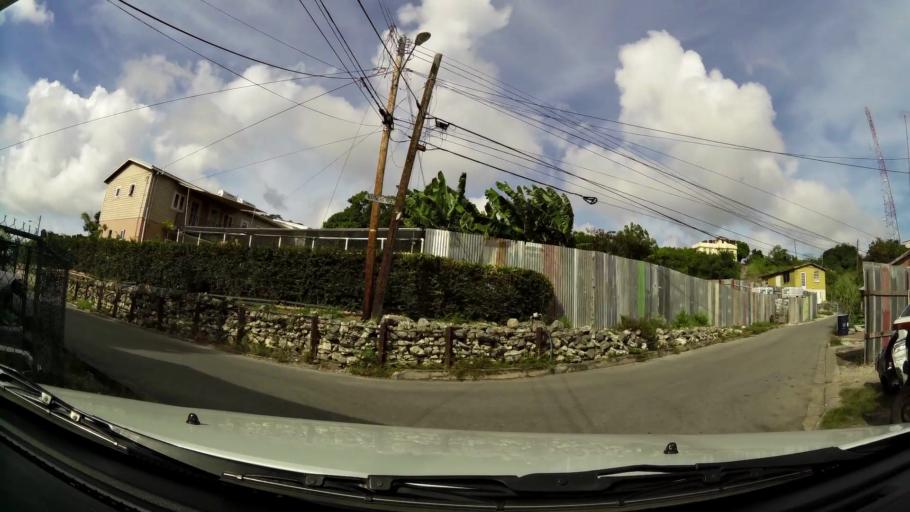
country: BB
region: Saint Michael
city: Bridgetown
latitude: 13.0879
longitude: -59.5909
